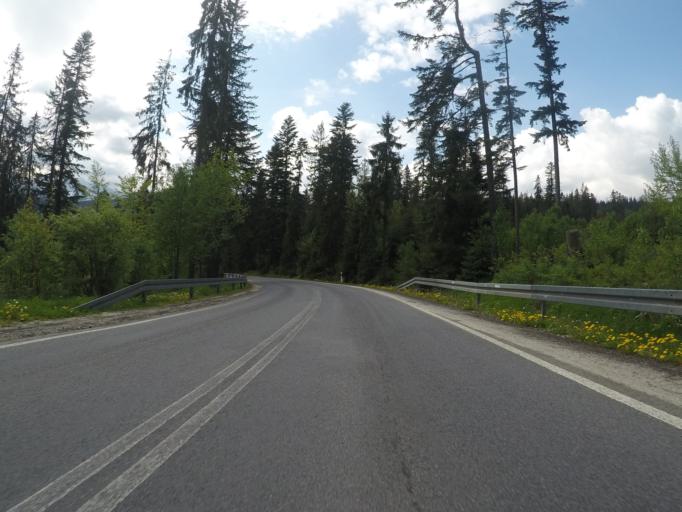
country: PL
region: Lesser Poland Voivodeship
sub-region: Powiat tatrzanski
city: Bukowina Tatrzanska
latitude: 49.2752
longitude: 20.1164
